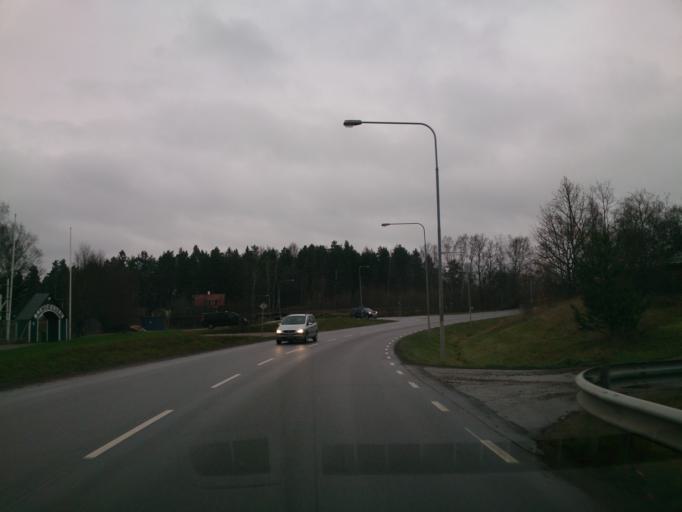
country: SE
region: OEstergoetland
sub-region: Linkopings Kommun
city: Linghem
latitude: 58.4345
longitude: 15.7804
